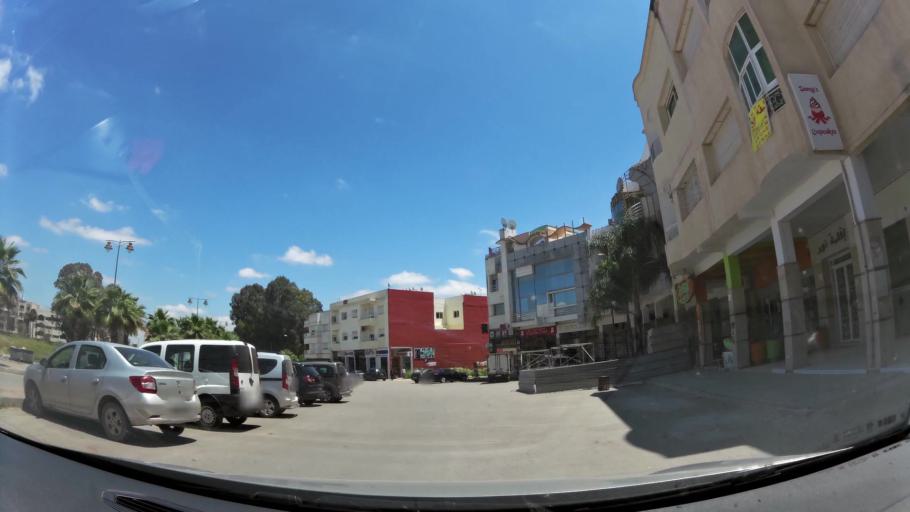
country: MA
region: Fes-Boulemane
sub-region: Fes
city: Fes
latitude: 34.0262
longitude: -5.0001
